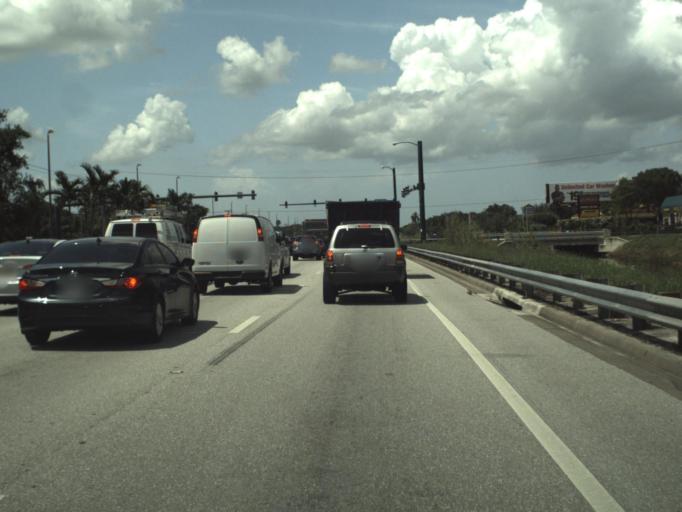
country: US
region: Florida
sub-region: Broward County
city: Parkland
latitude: 26.3297
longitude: -80.2028
